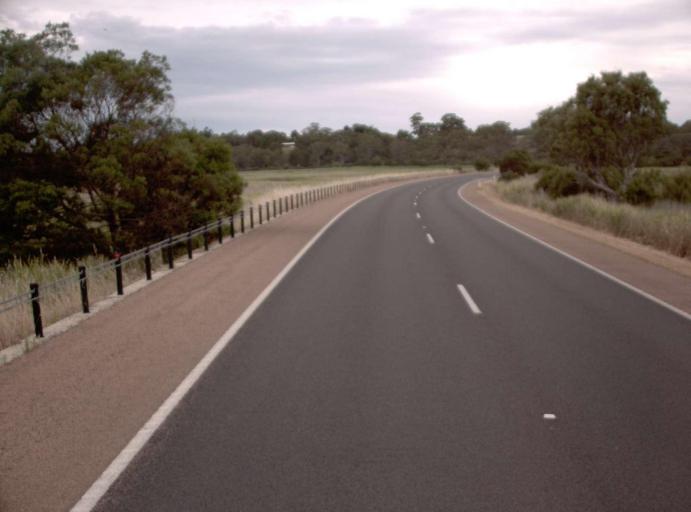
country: AU
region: Victoria
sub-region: East Gippsland
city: Bairnsdale
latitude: -37.8839
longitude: 147.6588
